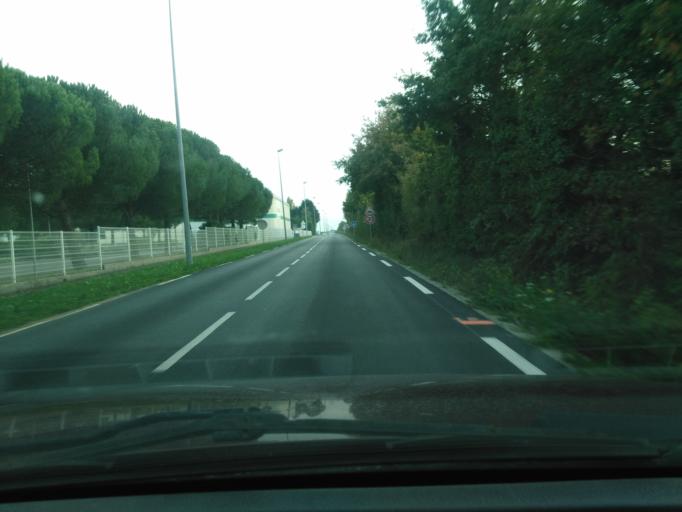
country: FR
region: Pays de la Loire
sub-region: Departement de la Vendee
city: Mouilleron-le-Captif
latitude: 46.7277
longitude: -1.4328
